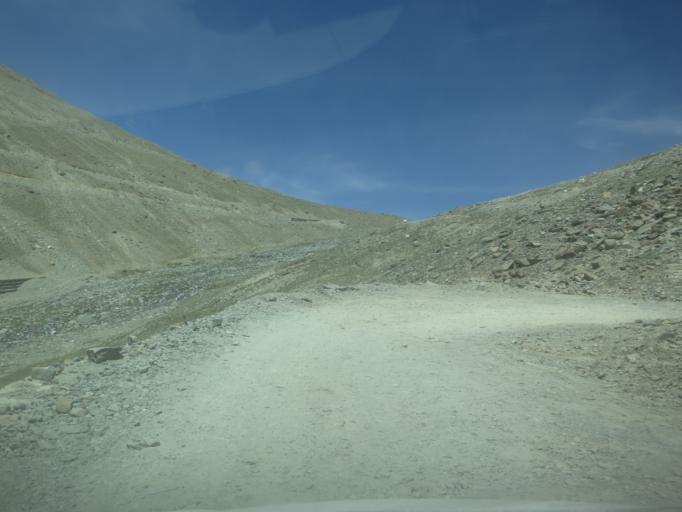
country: IN
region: Himachal Pradesh
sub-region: Kulu
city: Manali
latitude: 32.3870
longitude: 77.6231
